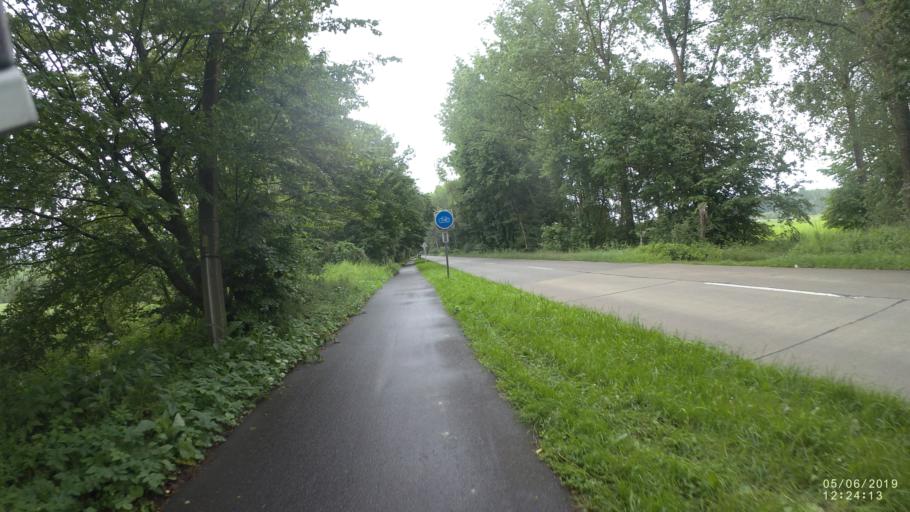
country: BE
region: Flanders
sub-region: Provincie Oost-Vlaanderen
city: Moerbeke
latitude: 51.1569
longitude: 3.9488
